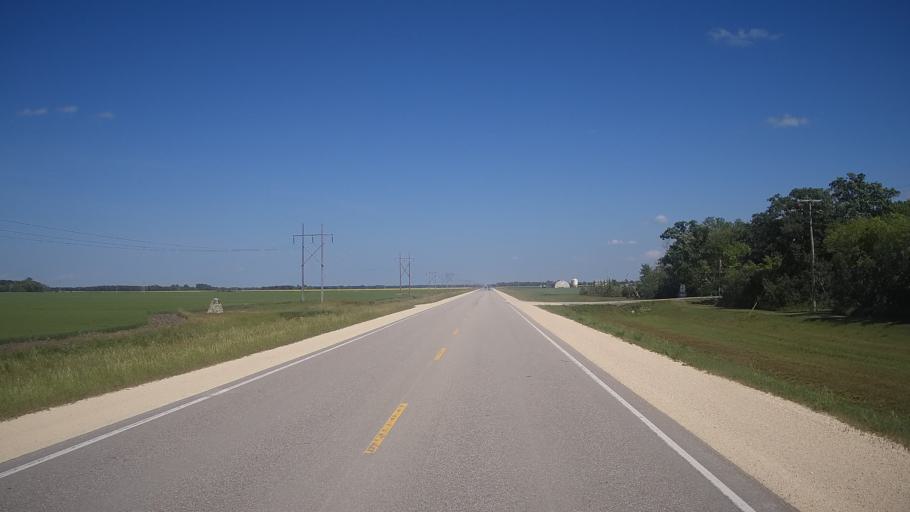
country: CA
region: Manitoba
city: Stonewall
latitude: 50.1227
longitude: -97.4242
